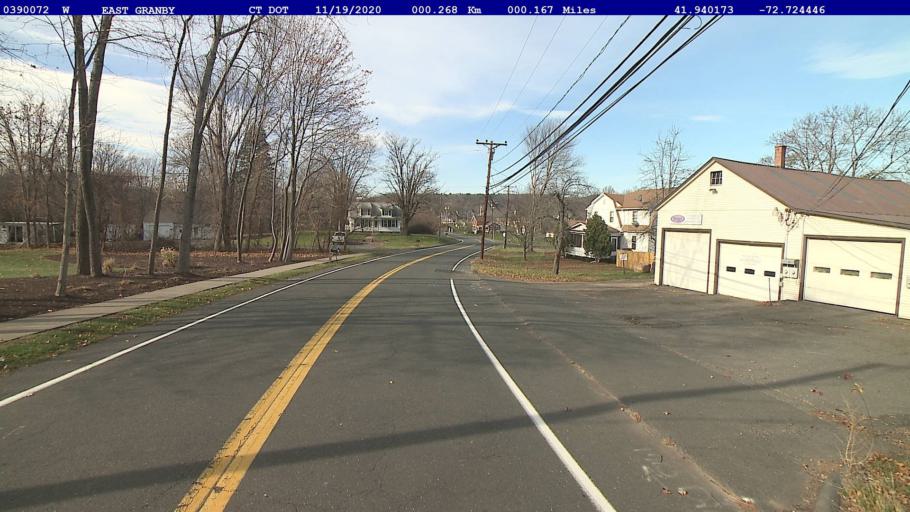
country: US
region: Connecticut
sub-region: Hartford County
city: Tariffville
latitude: 41.9402
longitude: -72.7245
